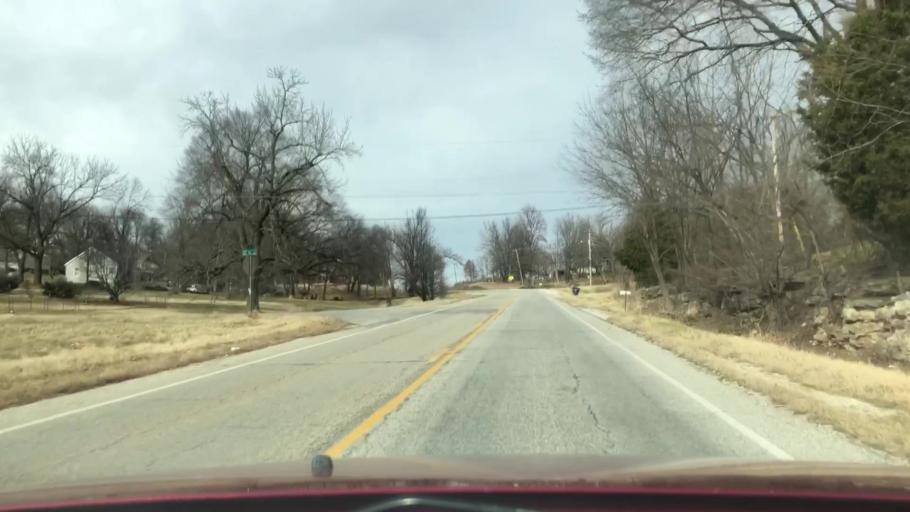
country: US
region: Missouri
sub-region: Greene County
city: Springfield
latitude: 37.2770
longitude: -93.2632
